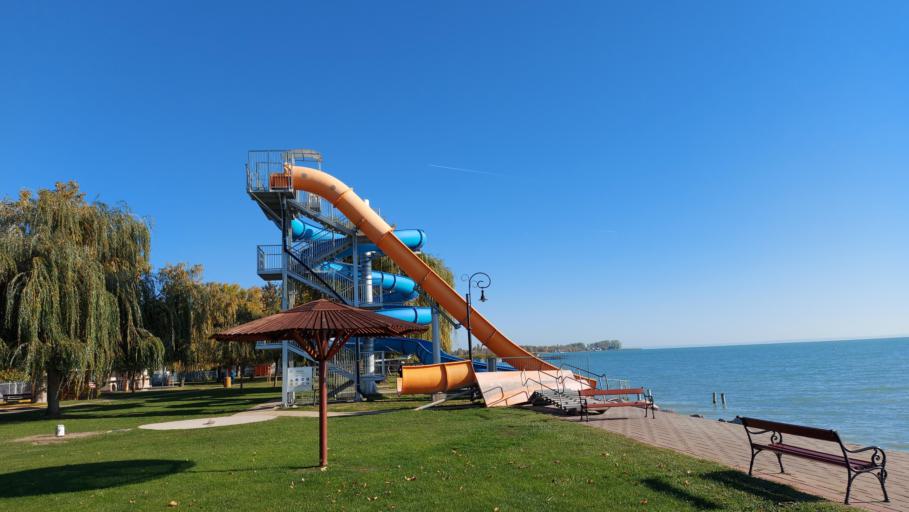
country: HU
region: Veszprem
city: Csopak
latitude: 46.9689
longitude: 17.9361
